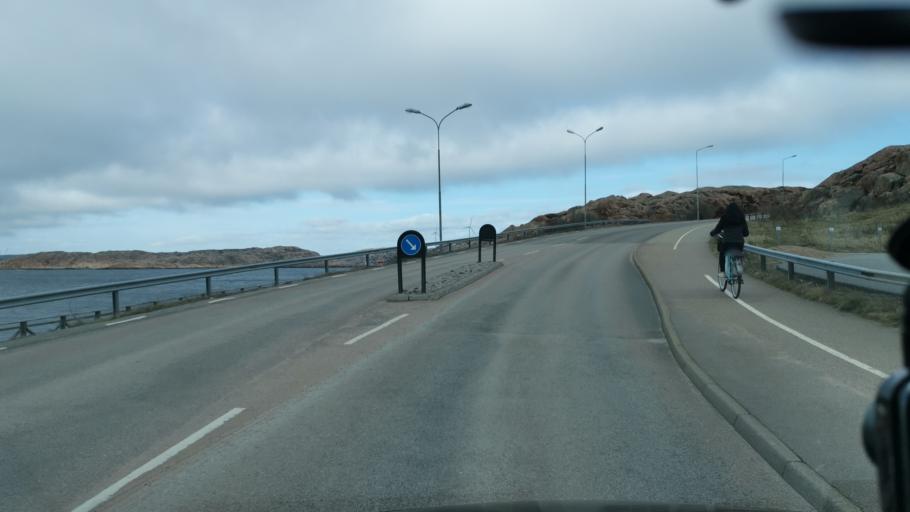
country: SE
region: Vaestra Goetaland
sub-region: Lysekils Kommun
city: Lysekil
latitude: 58.2800
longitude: 11.4267
